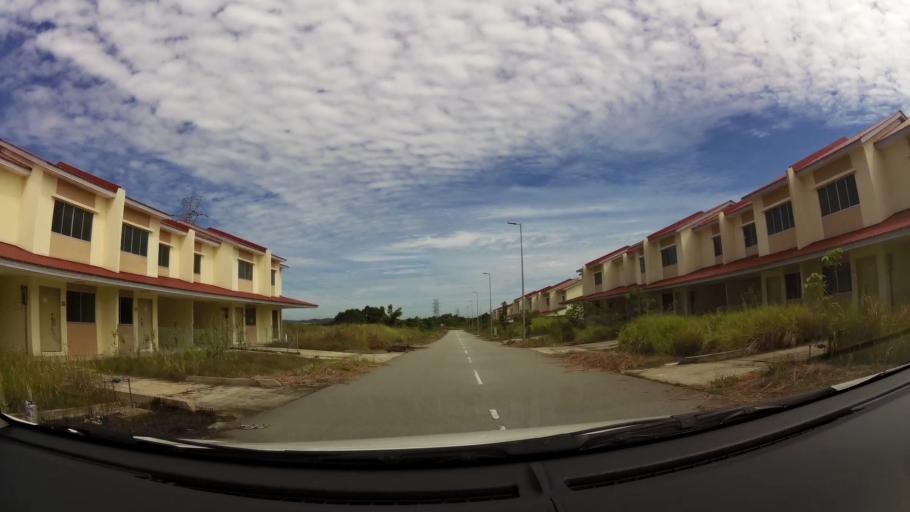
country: BN
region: Brunei and Muara
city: Bandar Seri Begawan
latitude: 4.9718
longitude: 115.0034
